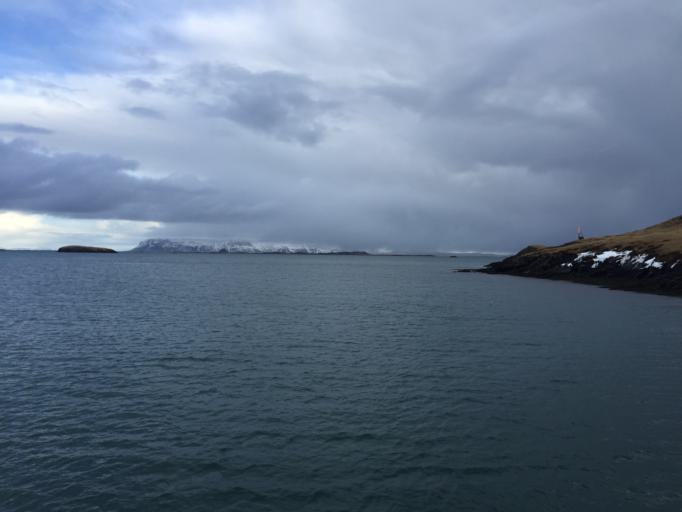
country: IS
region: West
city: Stykkisholmur
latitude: 65.0803
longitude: -22.7295
